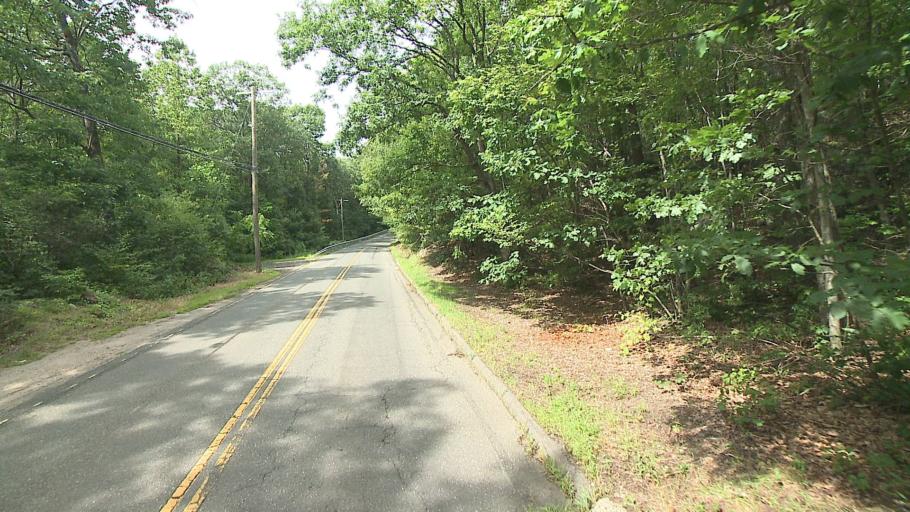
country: US
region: Connecticut
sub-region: Litchfield County
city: Plymouth
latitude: 41.6251
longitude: -73.0497
